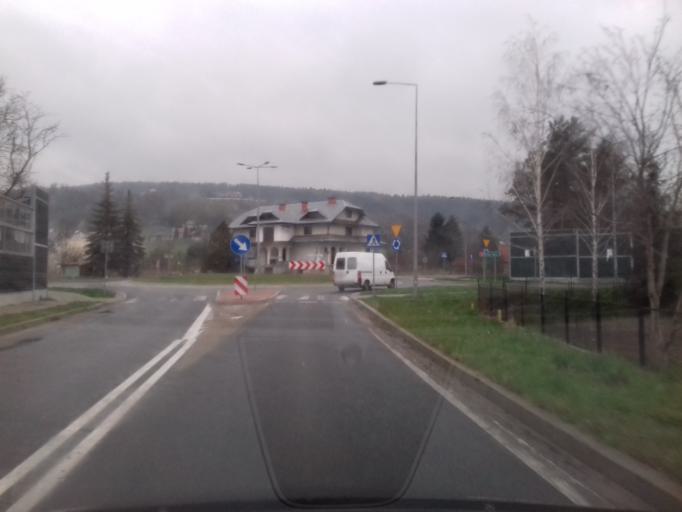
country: PL
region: Lesser Poland Voivodeship
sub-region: Powiat nowosadecki
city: Chelmiec
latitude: 49.6304
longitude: 20.6522
